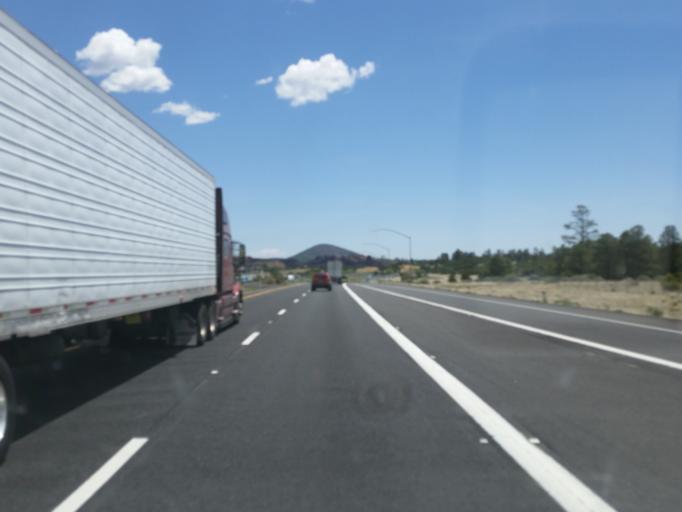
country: US
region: Arizona
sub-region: Coconino County
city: Flagstaff
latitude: 35.2172
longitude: -111.5785
